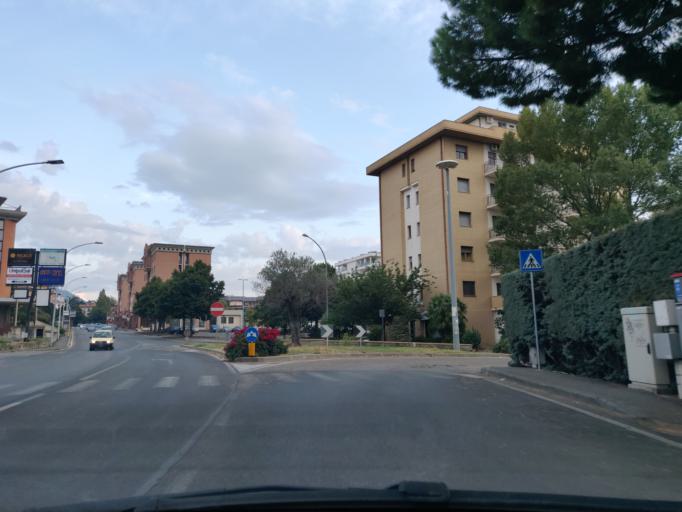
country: IT
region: Latium
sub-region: Provincia di Viterbo
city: Viterbo
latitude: 42.4278
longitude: 12.1006
